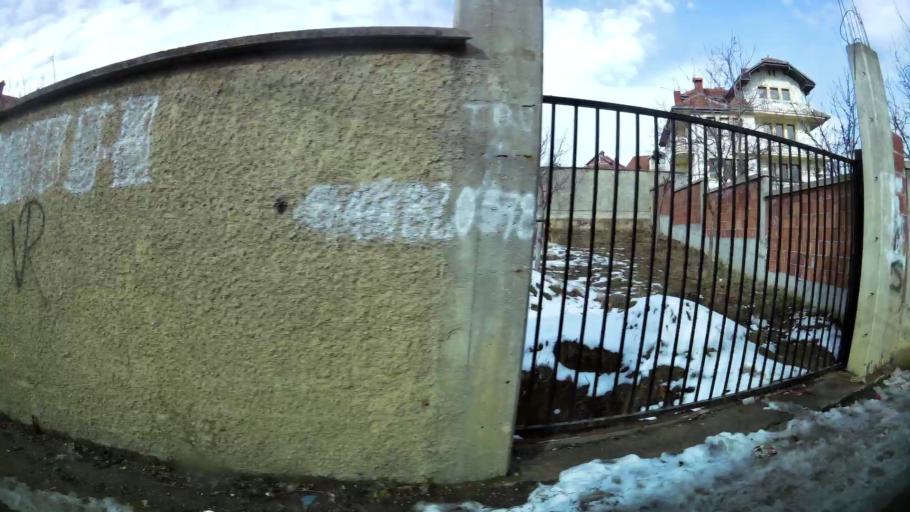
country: XK
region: Pristina
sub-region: Komuna e Prishtines
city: Pristina
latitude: 42.6832
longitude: 21.1547
